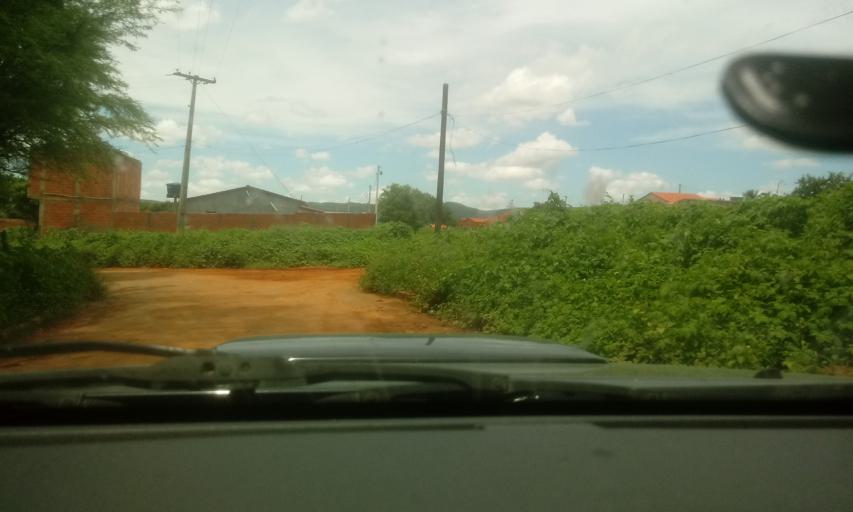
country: BR
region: Bahia
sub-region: Riacho De Santana
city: Riacho de Santana
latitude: -13.6039
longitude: -42.9471
